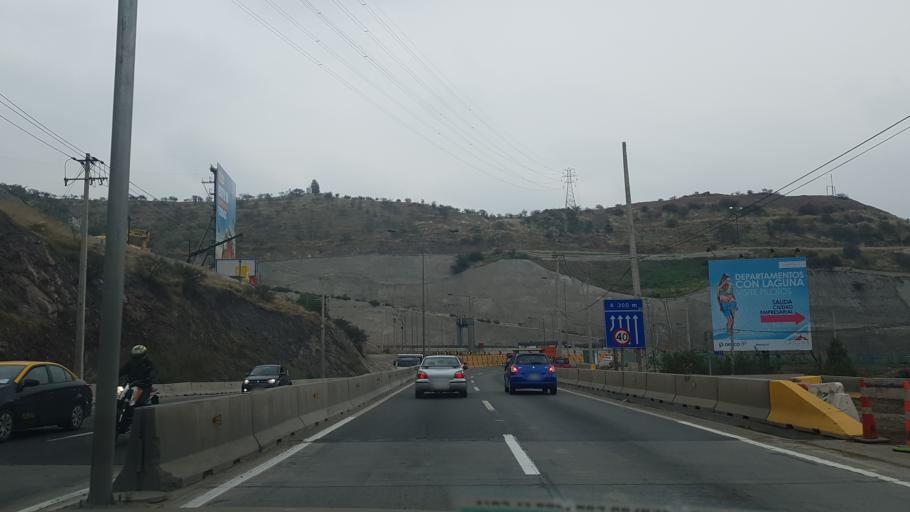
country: CL
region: Santiago Metropolitan
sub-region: Provincia de Santiago
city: Santiago
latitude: -33.3979
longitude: -70.6135
